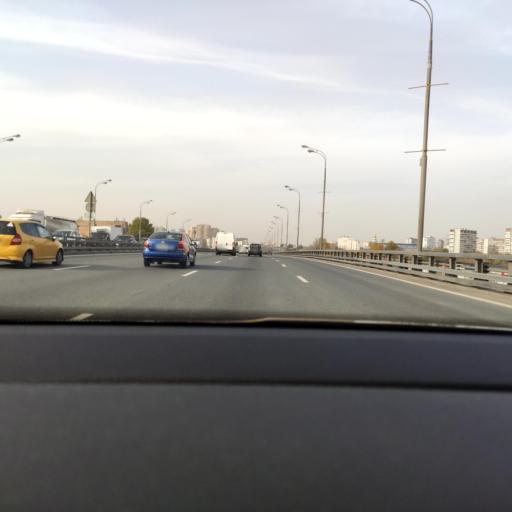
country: RU
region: Moscow
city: Tekstil'shchiki
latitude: 55.7272
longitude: 37.7119
